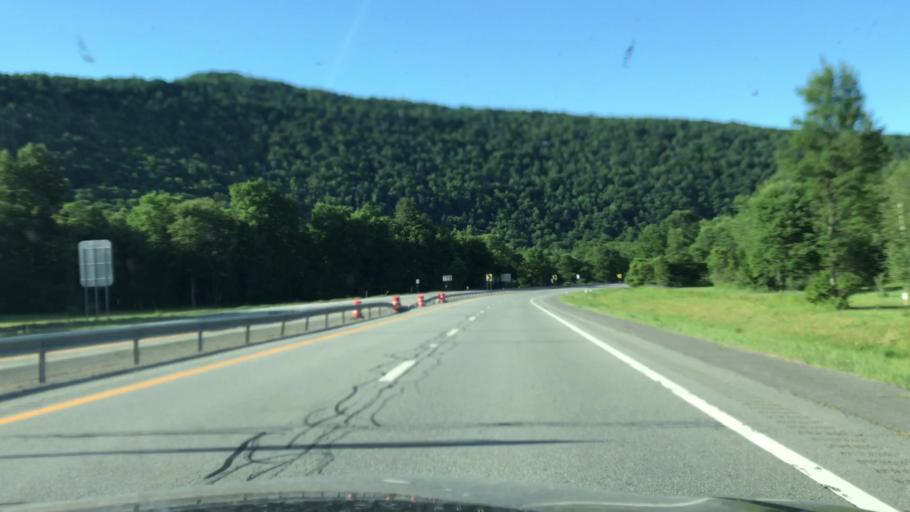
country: US
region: New York
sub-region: Delaware County
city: Hancock
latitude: 41.9948
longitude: -75.1599
